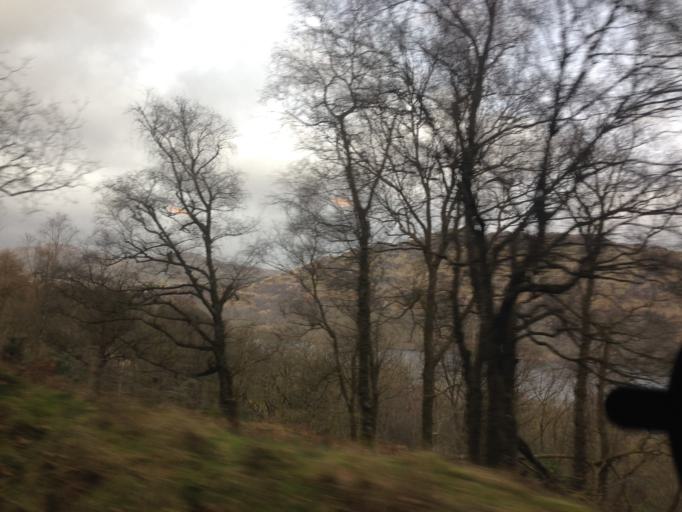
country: GB
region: Scotland
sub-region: Argyll and Bute
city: Garelochhead
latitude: 56.2174
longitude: -4.6994
